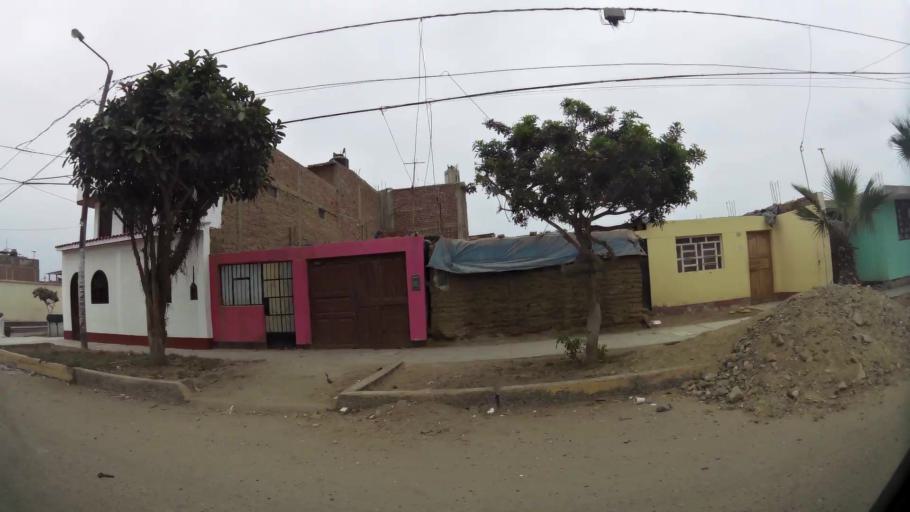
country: PE
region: La Libertad
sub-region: Provincia de Trujillo
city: Buenos Aires
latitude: -8.1451
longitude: -79.0490
